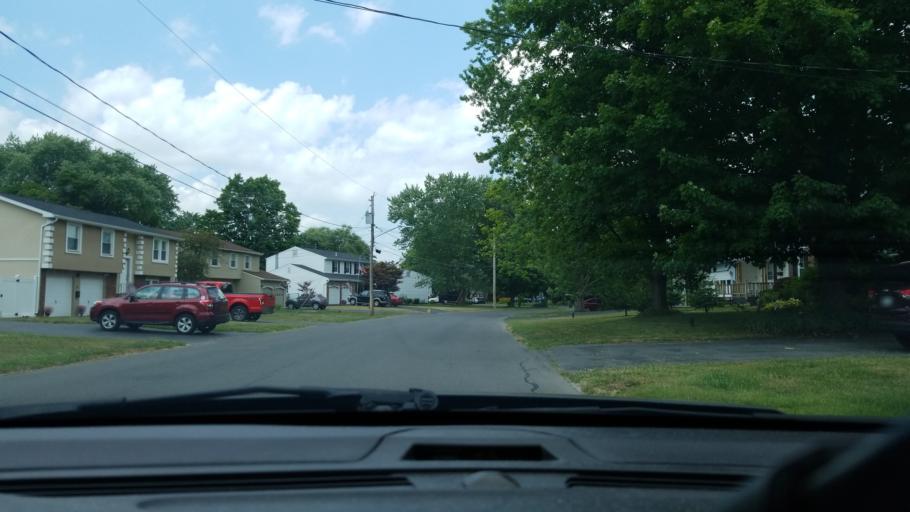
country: US
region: New York
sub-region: Onondaga County
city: Liverpool
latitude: 43.1422
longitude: -76.2117
